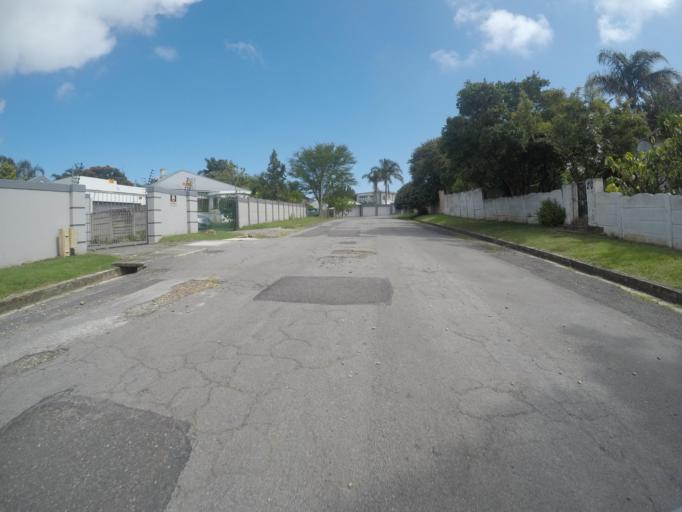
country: ZA
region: Eastern Cape
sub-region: Buffalo City Metropolitan Municipality
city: East London
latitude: -32.9777
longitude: 27.9079
